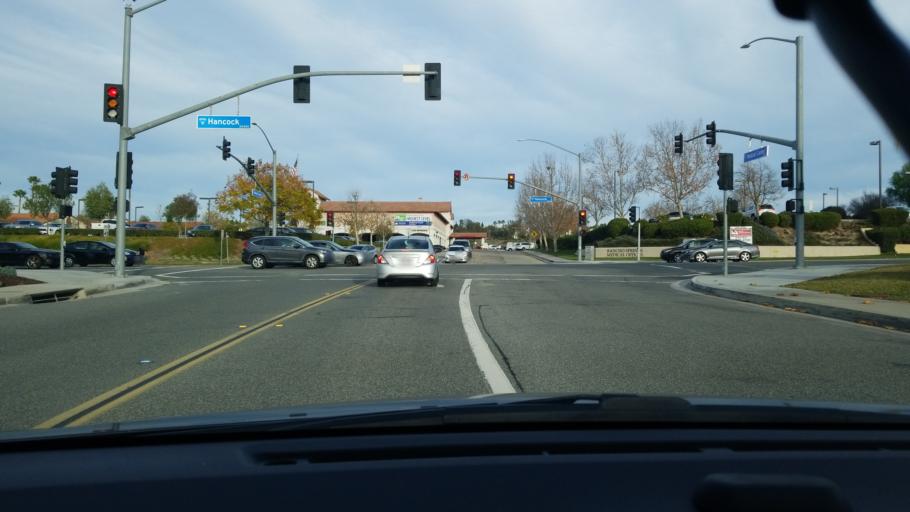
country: US
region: California
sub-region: Riverside County
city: Murrieta Hot Springs
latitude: 33.5576
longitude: -117.1853
